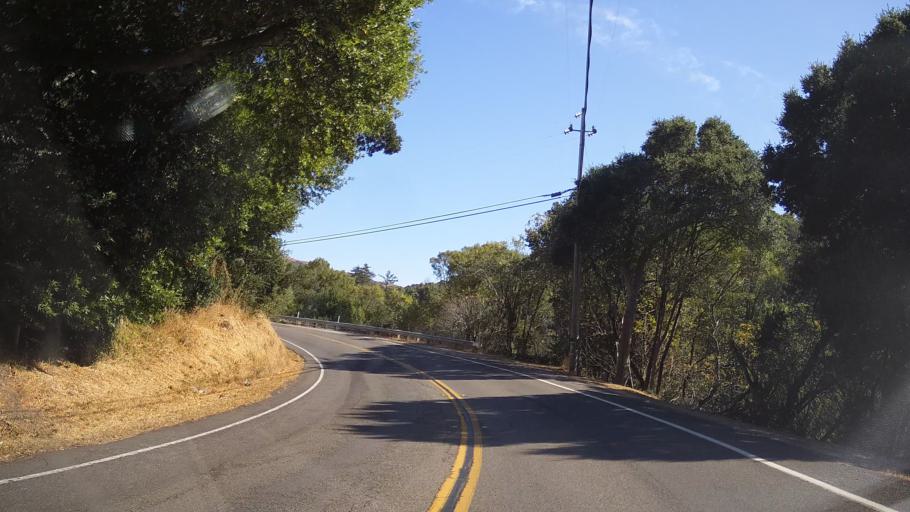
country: US
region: California
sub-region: Marin County
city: Inverness
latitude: 38.0789
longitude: -122.7776
